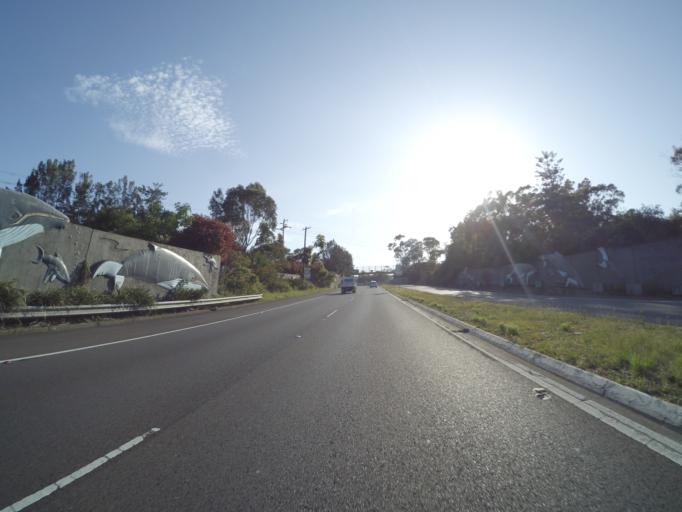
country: AU
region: New South Wales
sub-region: Sutherland Shire
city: Kirrawee
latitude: -34.0391
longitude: 151.0624
